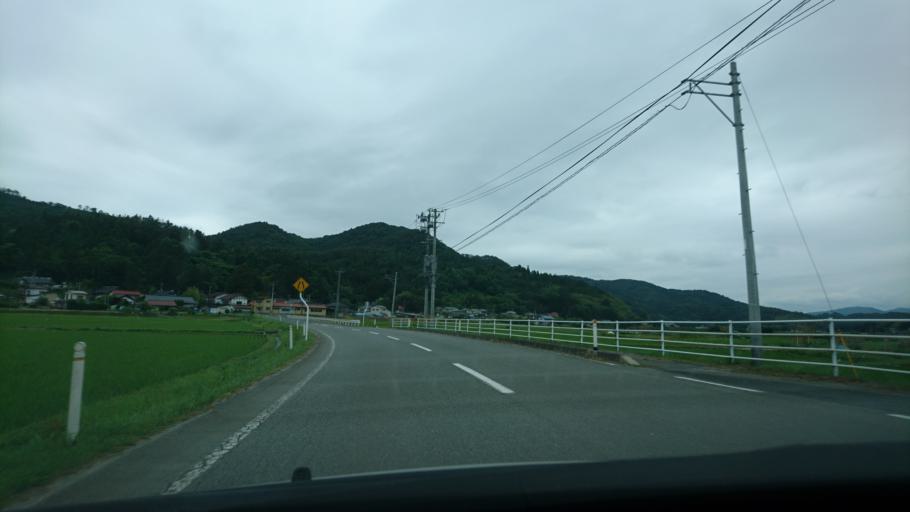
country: JP
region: Iwate
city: Ichinoseki
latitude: 38.9631
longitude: 141.2429
